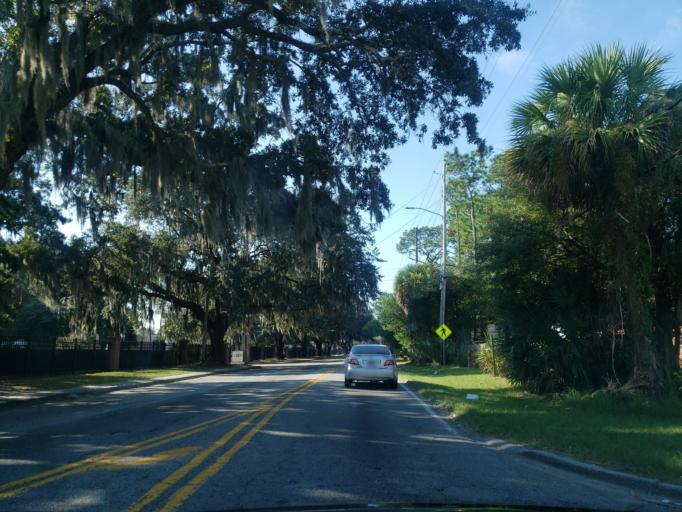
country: US
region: Georgia
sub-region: Chatham County
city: Thunderbolt
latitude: 32.0270
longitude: -81.0710
